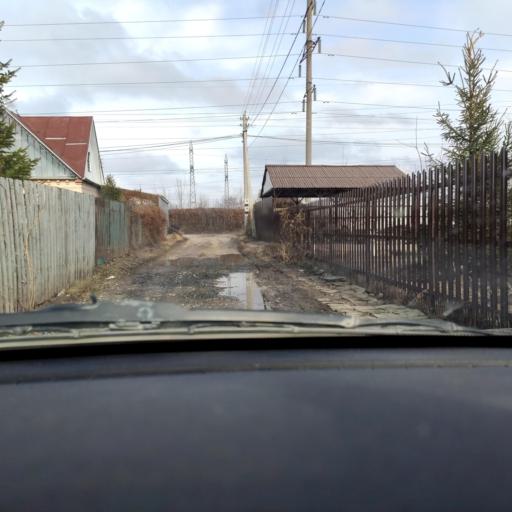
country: RU
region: Samara
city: Tol'yatti
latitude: 53.5877
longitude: 49.2910
